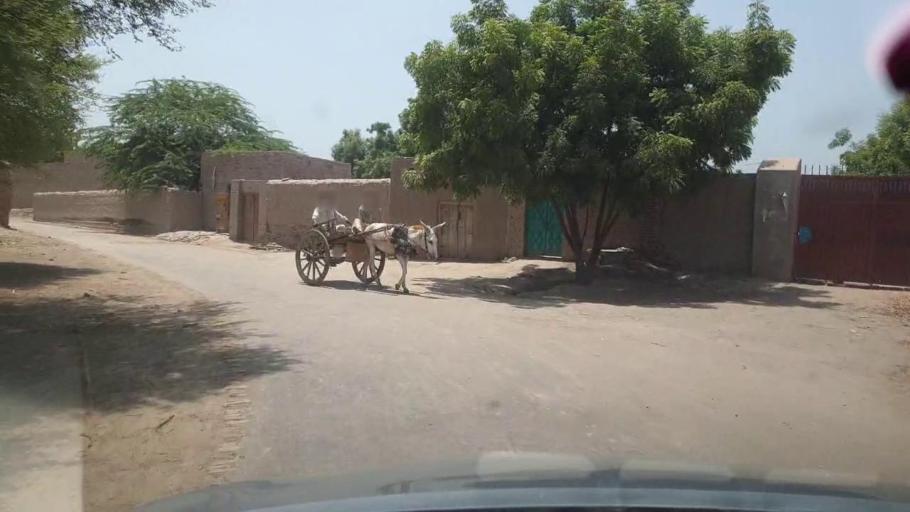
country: PK
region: Sindh
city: Hingorja
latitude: 27.2256
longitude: 68.3206
